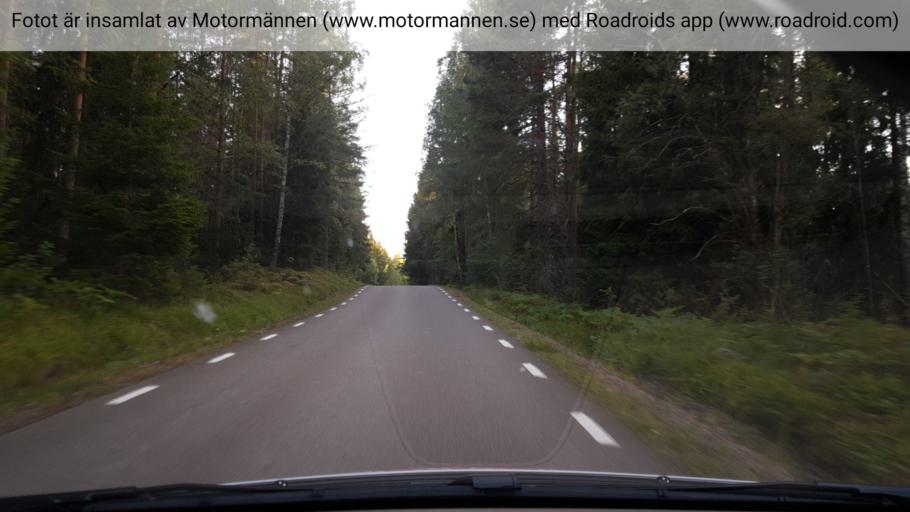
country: SE
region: Vaestmanland
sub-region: Surahammars Kommun
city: Ramnas
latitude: 59.7033
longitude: 16.0853
